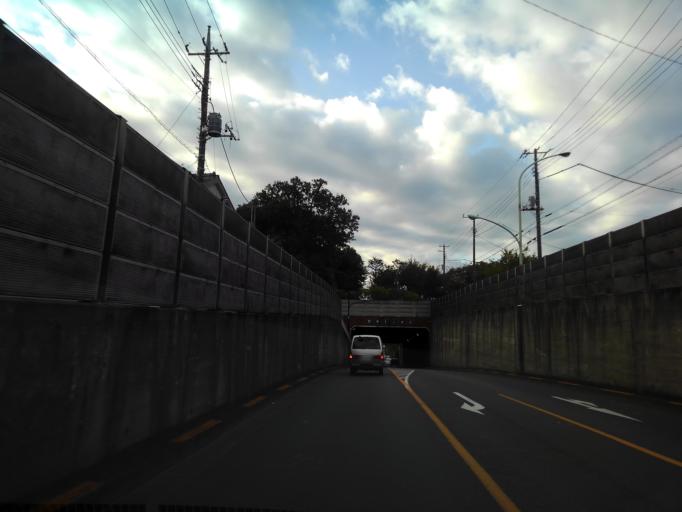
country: JP
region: Tokyo
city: Kokubunji
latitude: 35.6994
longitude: 139.4978
